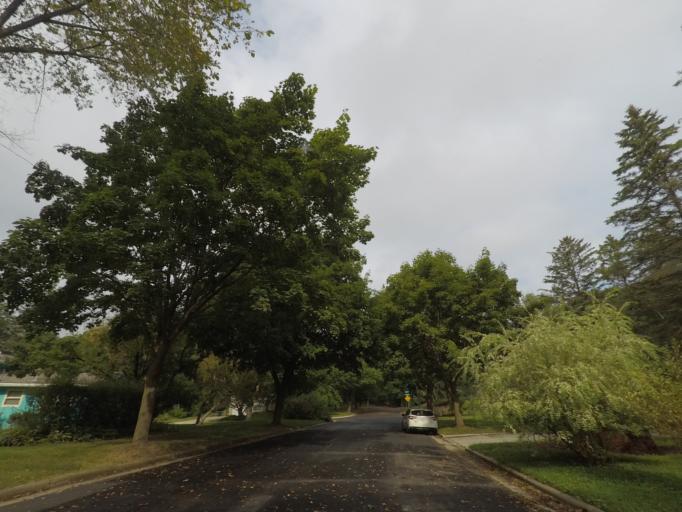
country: US
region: Wisconsin
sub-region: Dane County
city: Shorewood Hills
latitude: 43.0372
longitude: -89.4818
